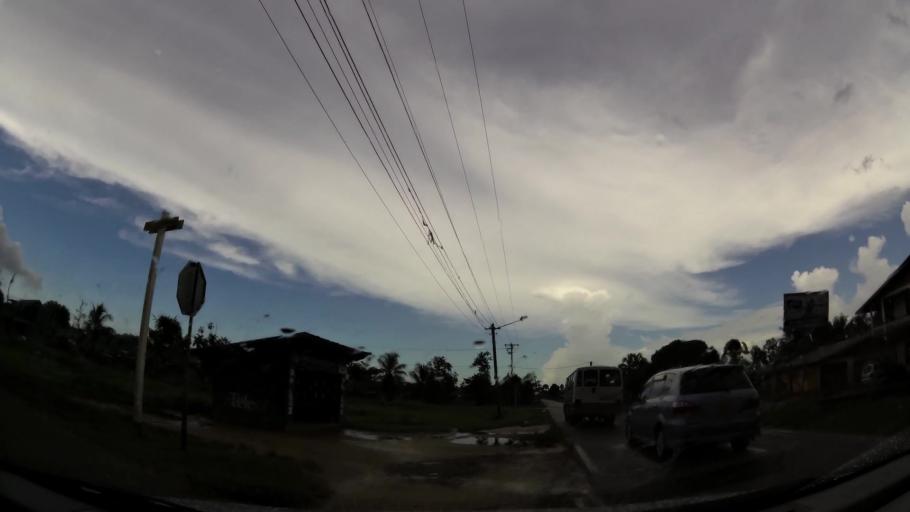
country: SR
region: Commewijne
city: Nieuw Amsterdam
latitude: 5.8855
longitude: -55.0609
